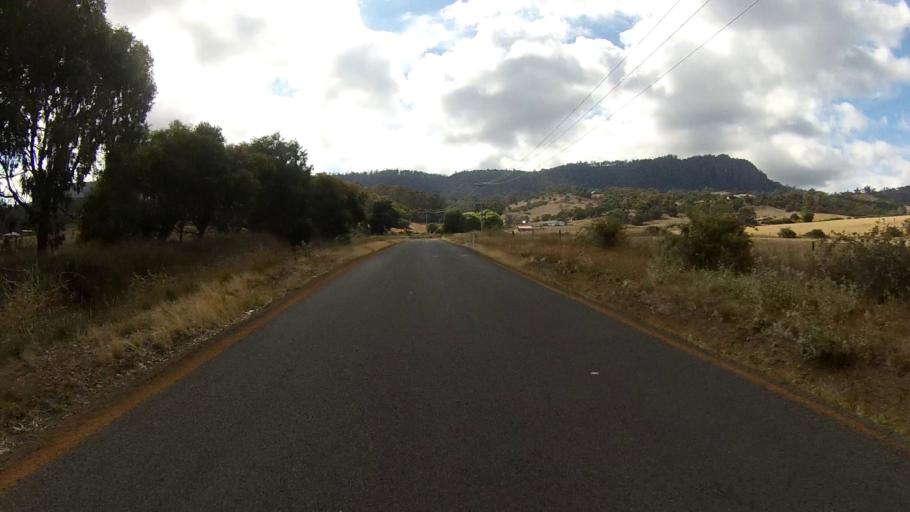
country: AU
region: Tasmania
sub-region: Brighton
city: Old Beach
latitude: -42.7594
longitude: 147.3025
